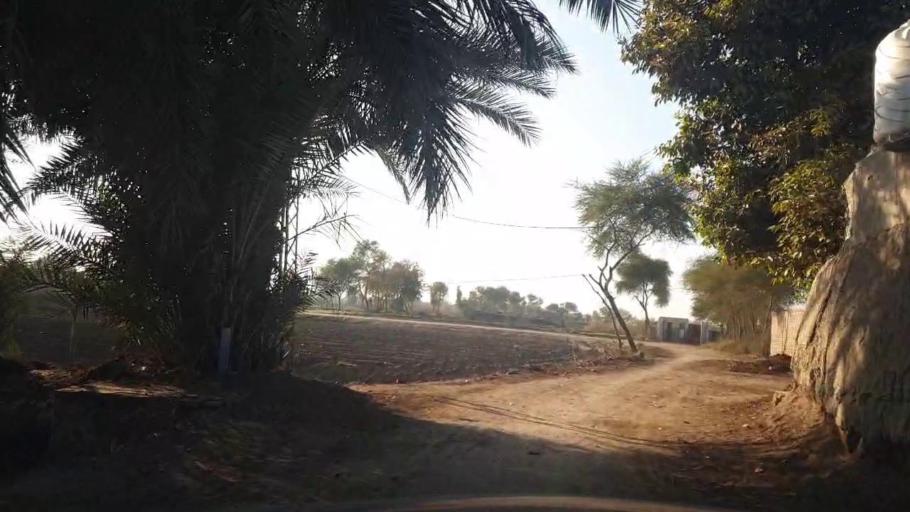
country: PK
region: Sindh
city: Mirpur Mathelo
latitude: 28.0048
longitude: 69.4729
